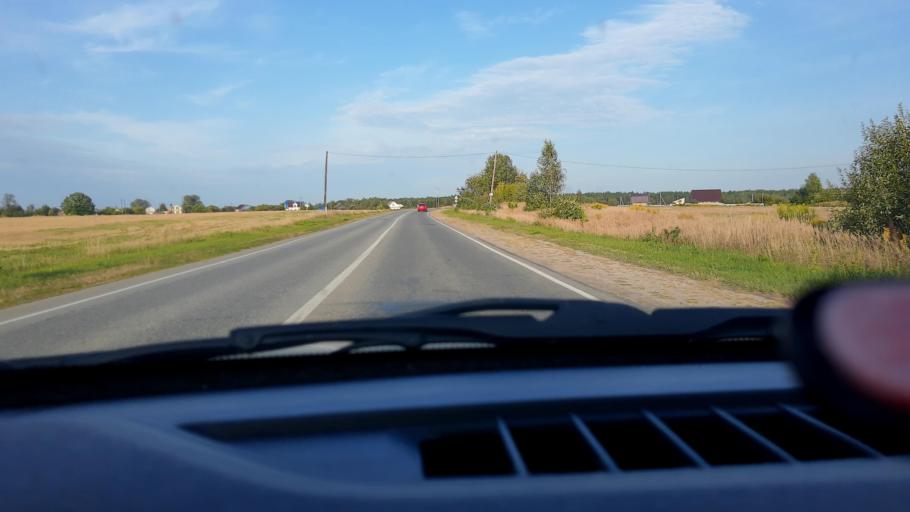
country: RU
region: Nizjnij Novgorod
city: Gorodets
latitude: 56.6482
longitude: 43.5156
